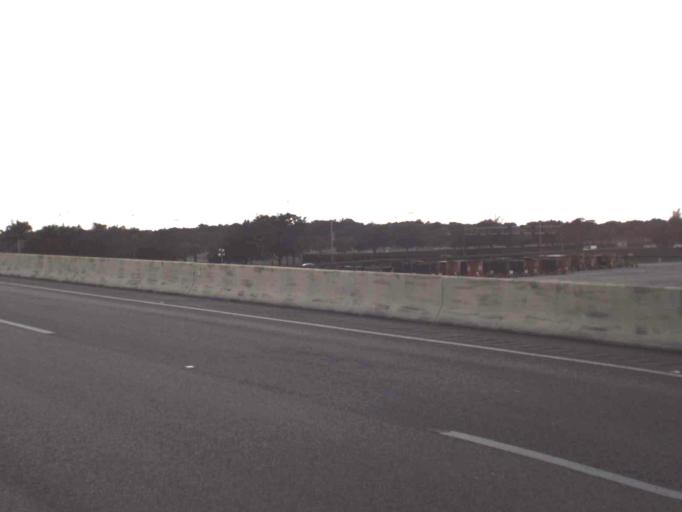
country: US
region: Florida
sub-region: Miami-Dade County
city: Lake Lucerne
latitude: 25.9577
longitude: -80.2294
